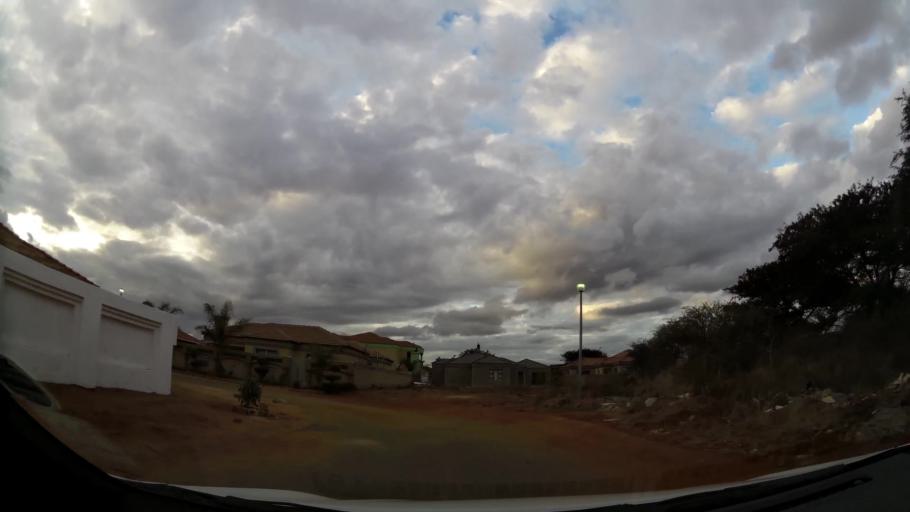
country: ZA
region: Limpopo
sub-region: Waterberg District Municipality
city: Mokopane
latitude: -24.2033
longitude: 28.9951
